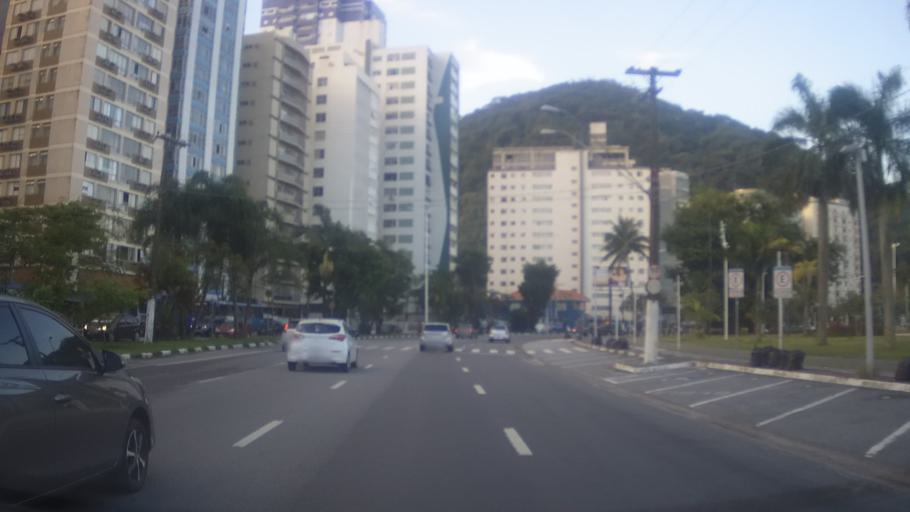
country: BR
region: Sao Paulo
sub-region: Sao Vicente
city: Sao Vicente
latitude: -23.9715
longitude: -46.3689
